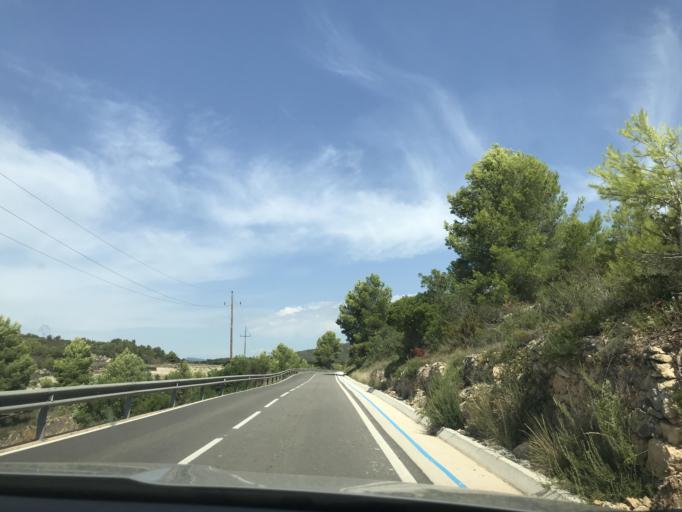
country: ES
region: Catalonia
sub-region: Provincia de Tarragona
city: Salomo
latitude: 41.2160
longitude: 1.3810
